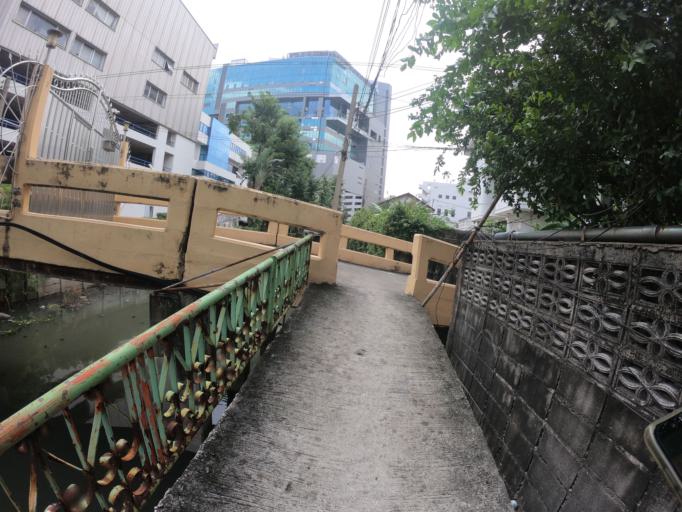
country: TH
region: Bangkok
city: Huai Khwang
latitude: 13.7540
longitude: 100.5716
